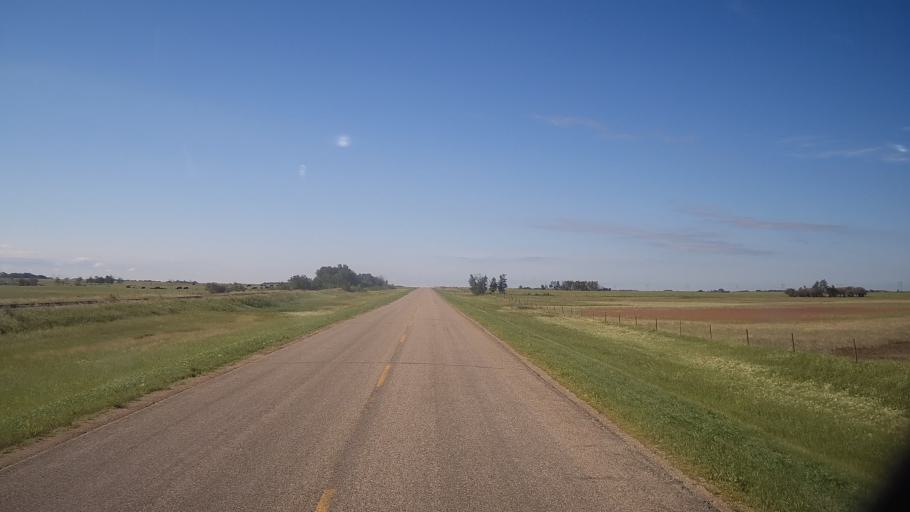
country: CA
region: Saskatchewan
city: Watrous
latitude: 51.7533
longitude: -105.2867
